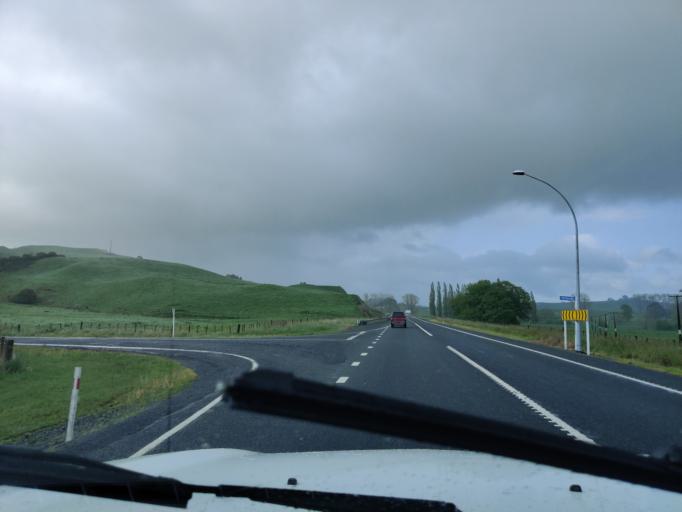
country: NZ
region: Waikato
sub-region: Matamata-Piako District
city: Matamata
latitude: -37.9653
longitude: 175.6889
